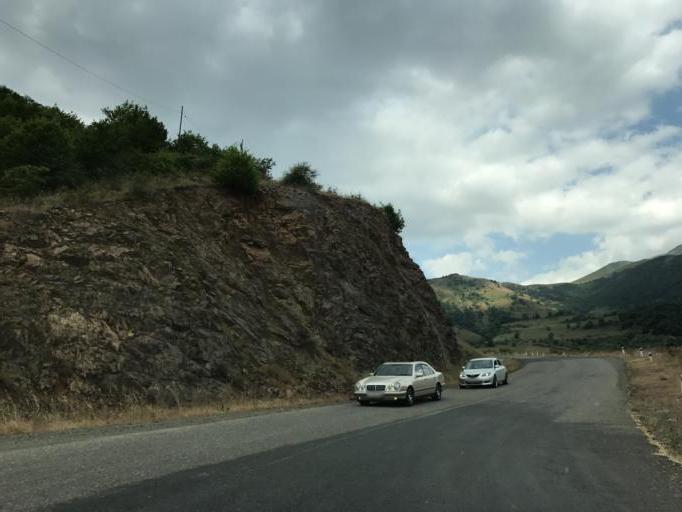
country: AZ
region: Lacin
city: Lacin
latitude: 39.6780
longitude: 46.6293
